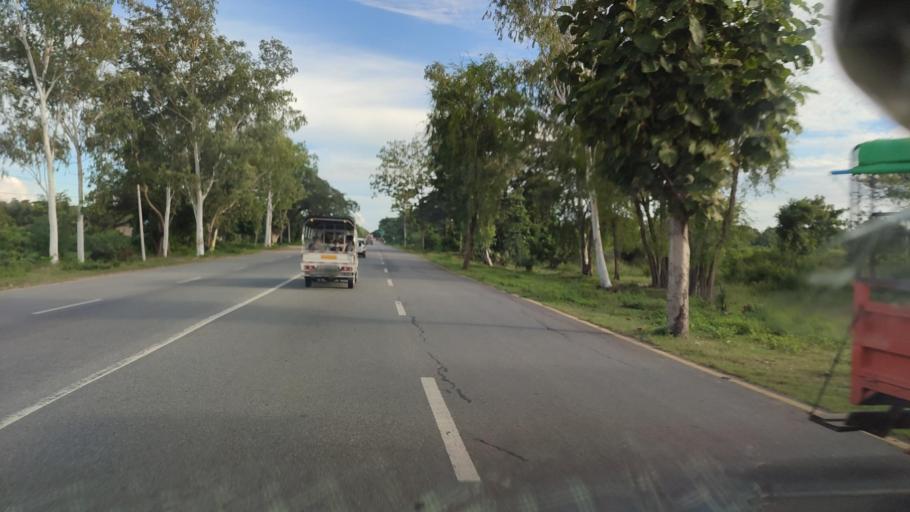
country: MM
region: Mandalay
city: Yamethin
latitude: 20.1642
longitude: 96.1900
